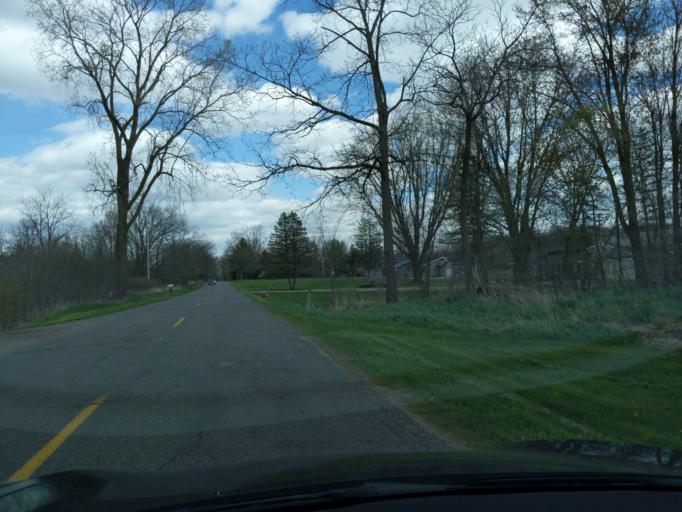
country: US
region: Michigan
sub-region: Ingham County
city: Holt
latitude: 42.6258
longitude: -84.5729
